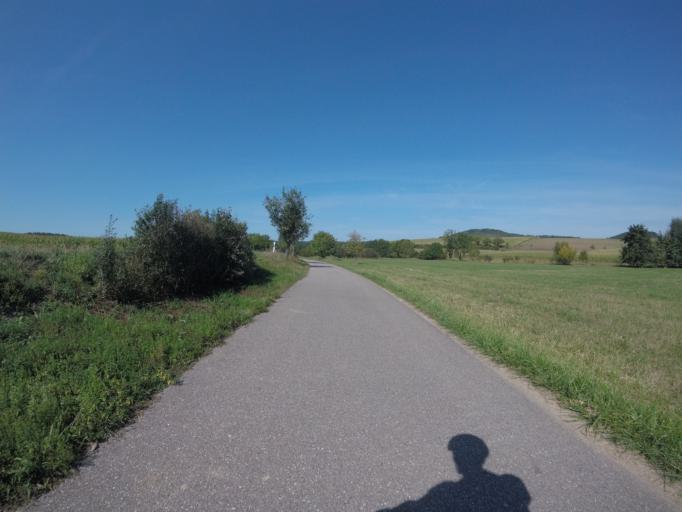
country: DE
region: Baden-Wuerttemberg
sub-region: Regierungsbezirk Stuttgart
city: Grossbottwar
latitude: 49.0095
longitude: 9.2777
